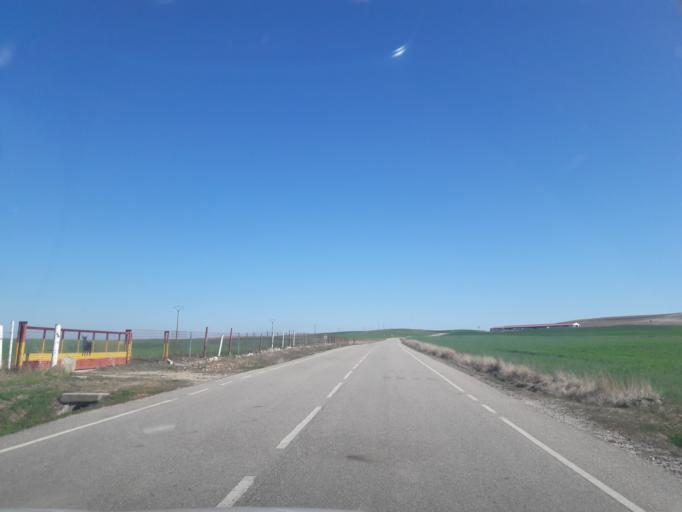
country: ES
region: Castille and Leon
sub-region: Provincia de Salamanca
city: Salmoral
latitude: 40.8074
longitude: -5.2187
